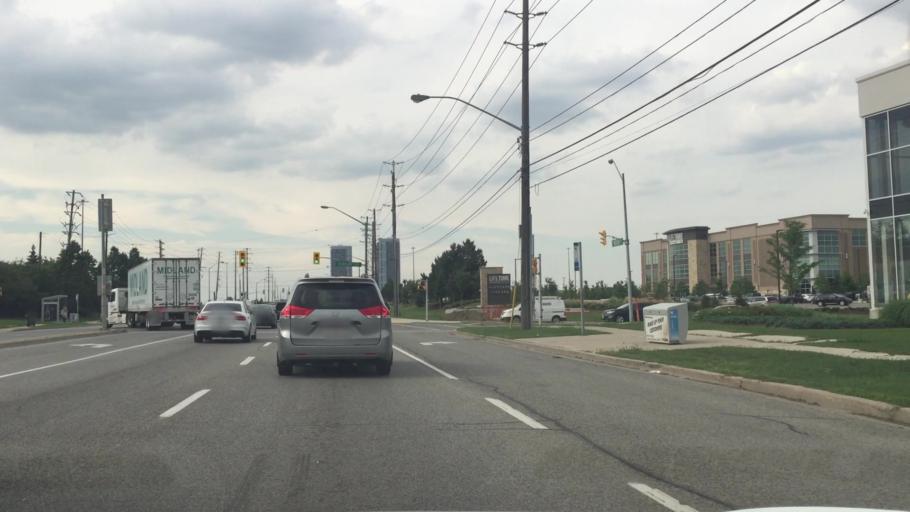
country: CA
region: Ontario
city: Concord
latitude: 43.7769
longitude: -79.5446
